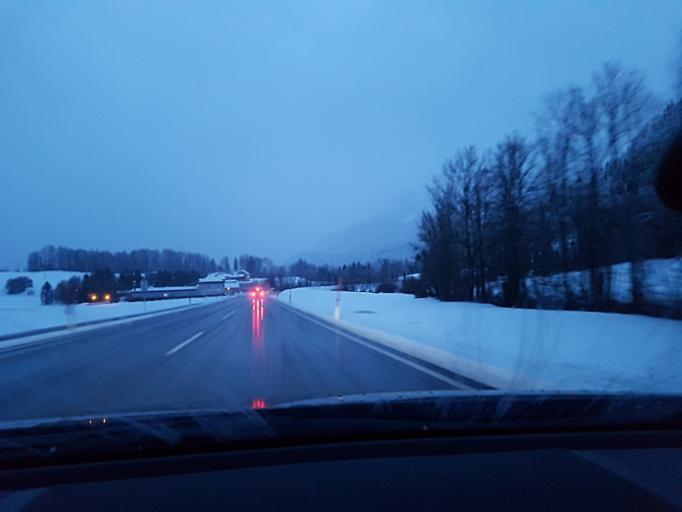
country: AT
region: Salzburg
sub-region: Politischer Bezirk Salzburg-Umgebung
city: Sankt Gilgen
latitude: 47.7814
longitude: 13.3459
